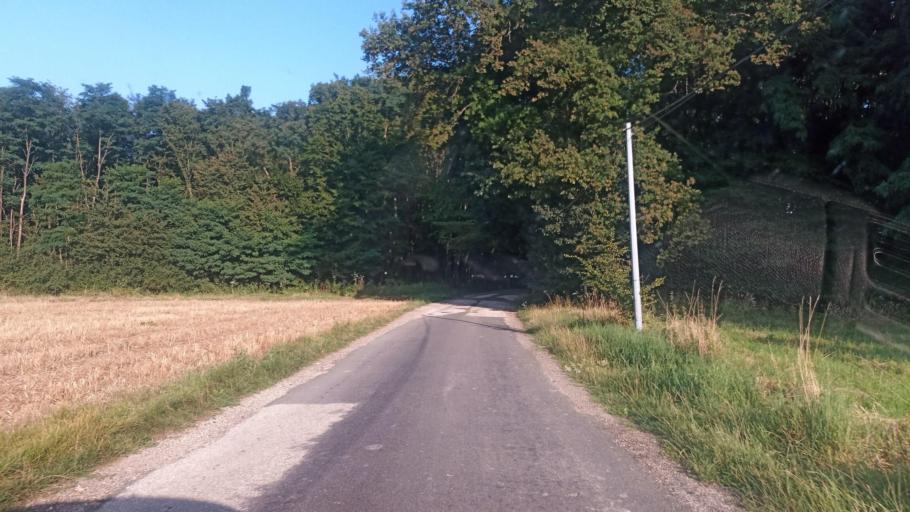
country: FR
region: Bourgogne
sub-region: Departement de l'Yonne
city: Pont-sur-Yonne
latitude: 48.2593
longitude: 3.1751
